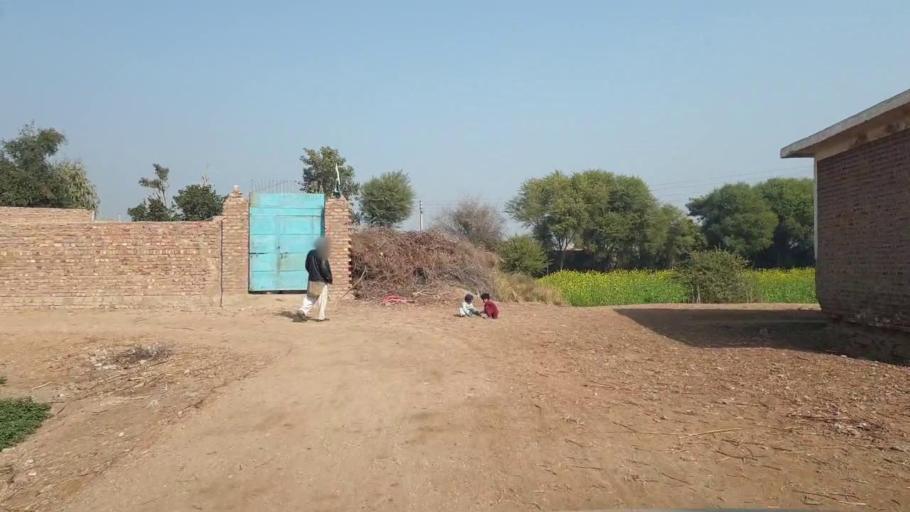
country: PK
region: Sindh
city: Sakrand
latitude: 26.0071
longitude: 68.3634
